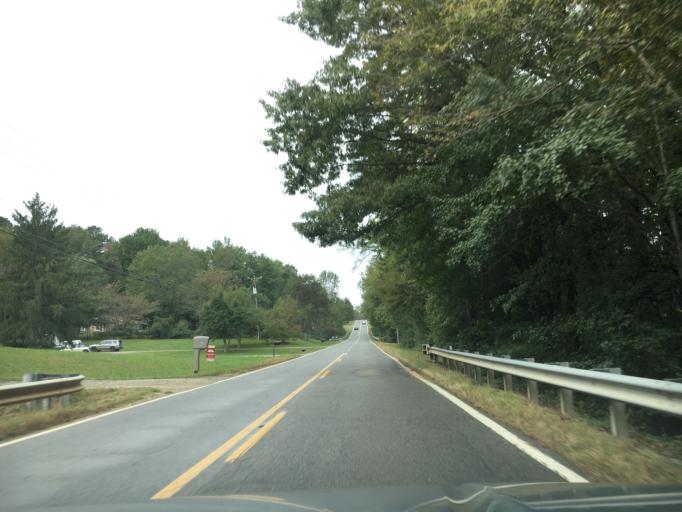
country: US
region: Virginia
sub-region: Goochland County
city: Goochland
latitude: 37.7639
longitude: -77.8796
